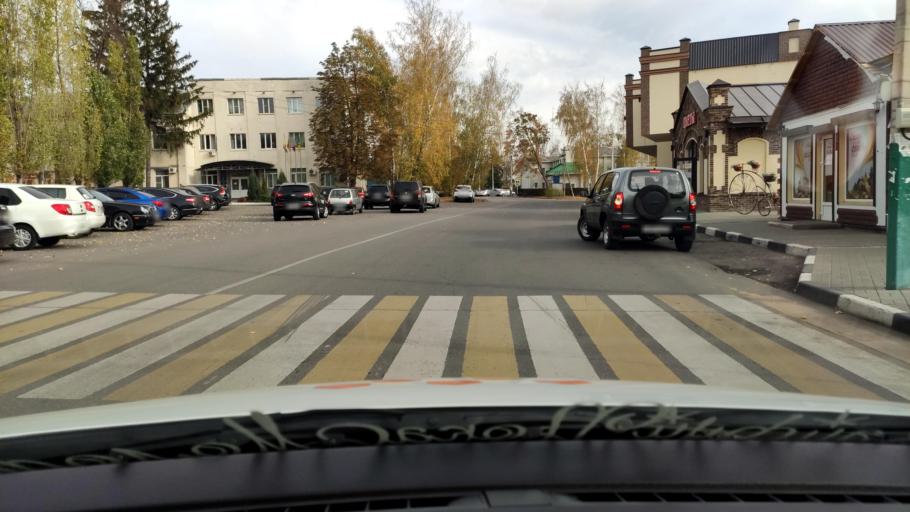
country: RU
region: Voronezj
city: Ramon'
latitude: 51.9140
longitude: 39.3396
